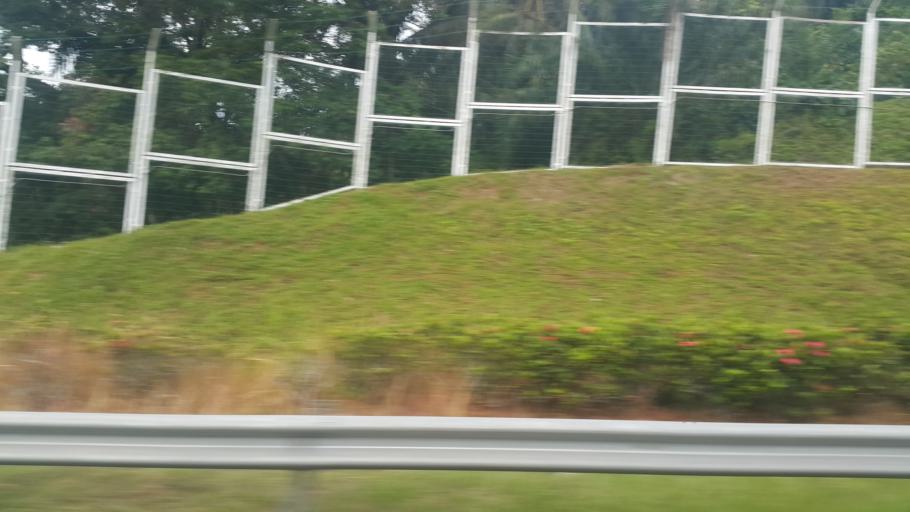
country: MY
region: Johor
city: Pekan Nenas
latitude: 1.3689
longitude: 103.6127
